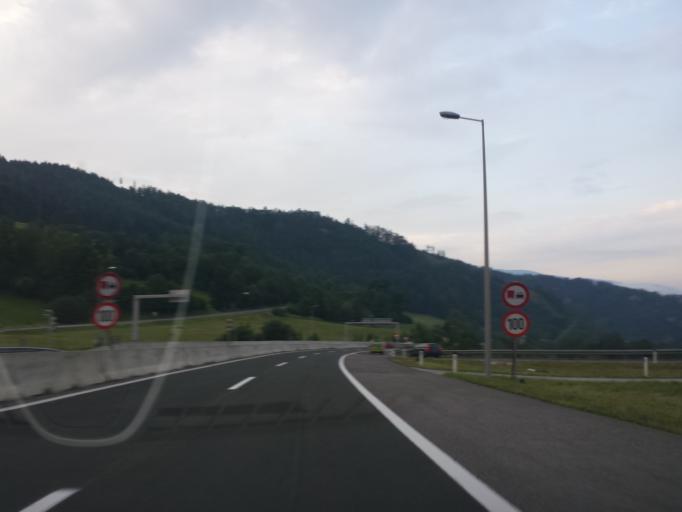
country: AT
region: Lower Austria
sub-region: Politischer Bezirk Neunkirchen
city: Semmering
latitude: 47.6406
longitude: 15.8499
